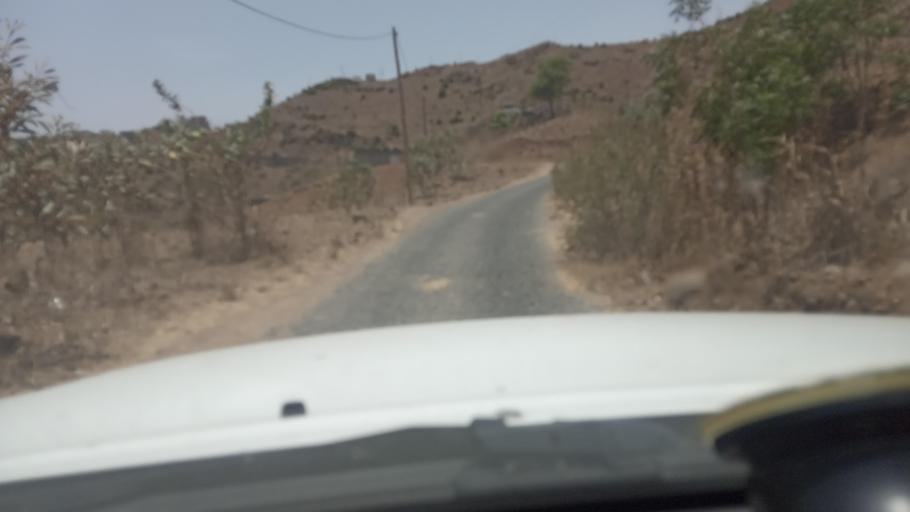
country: CV
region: Sao Salvador do Mundo
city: Picos
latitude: 15.0925
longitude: -23.6481
